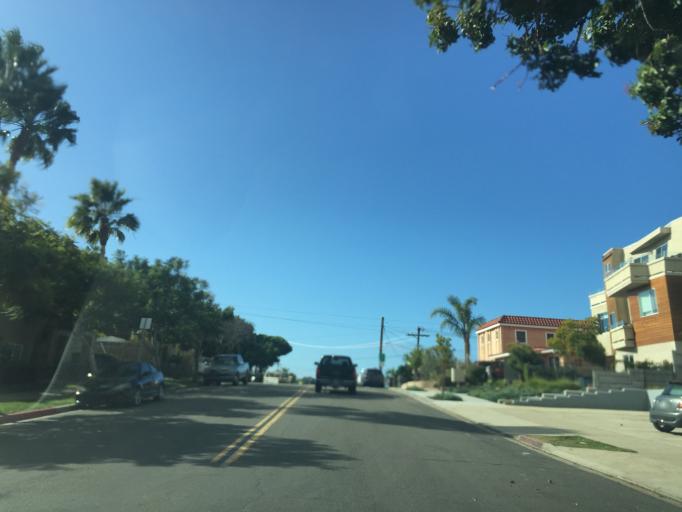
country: US
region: California
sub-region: San Diego County
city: La Jolla
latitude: 32.7938
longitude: -117.2400
